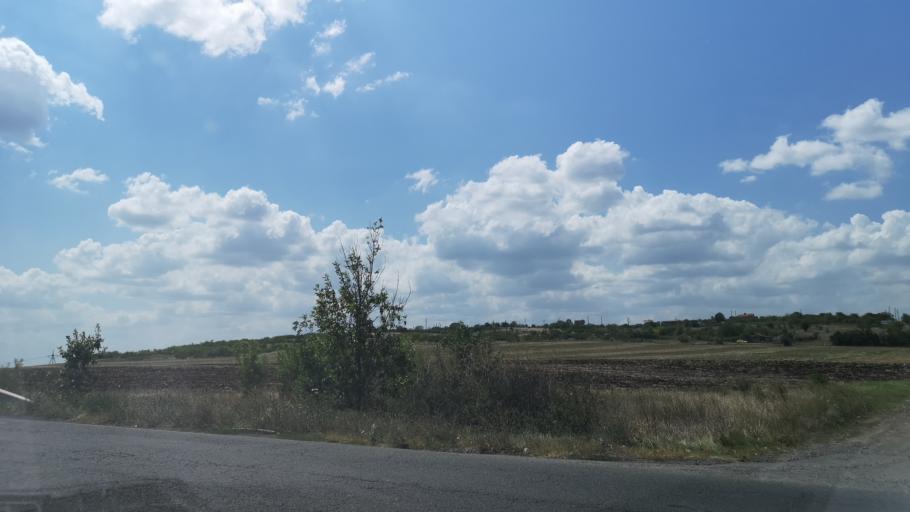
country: BG
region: Burgas
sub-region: Obshtina Kameno
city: Kameno
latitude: 42.6358
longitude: 27.3412
